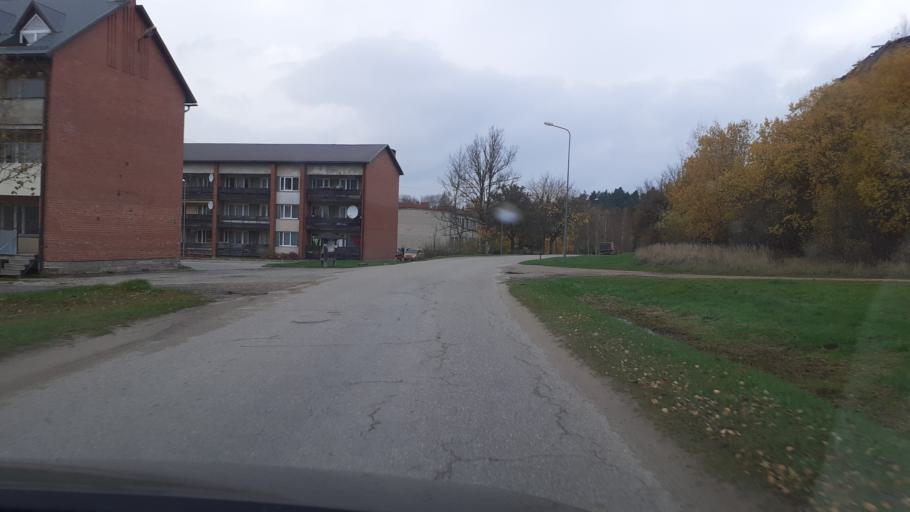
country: LV
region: Kuldigas Rajons
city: Kuldiga
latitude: 56.9839
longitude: 22.0194
